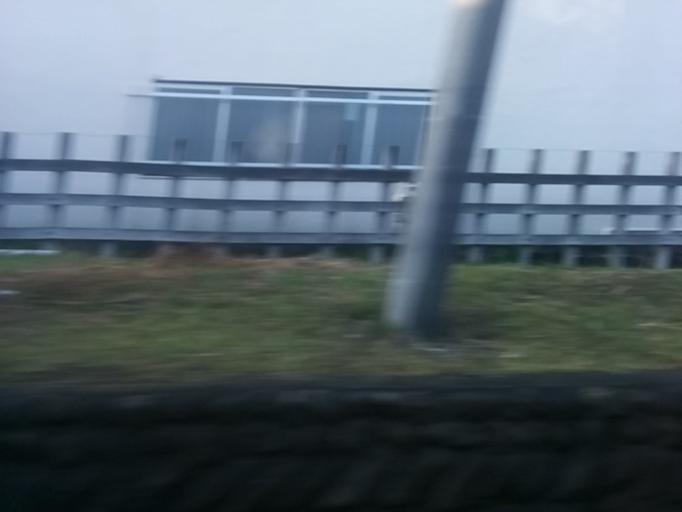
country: JP
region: Saitama
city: Wako
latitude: 35.7749
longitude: 139.6370
